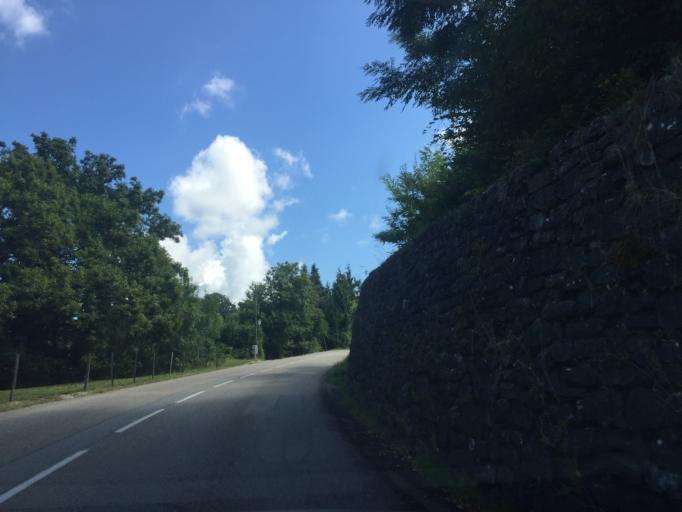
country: FR
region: Rhone-Alpes
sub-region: Departement de la Savoie
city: La Rochette
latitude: 45.4507
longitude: 6.1325
